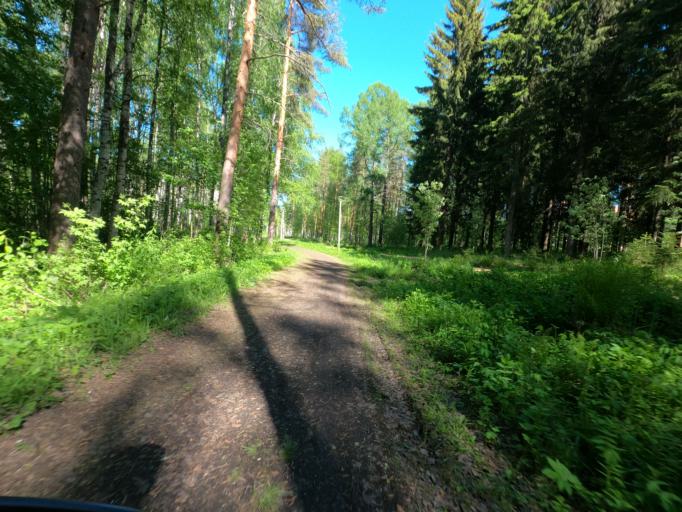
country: FI
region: North Karelia
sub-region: Joensuu
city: Joensuu
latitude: 62.6069
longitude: 29.7948
